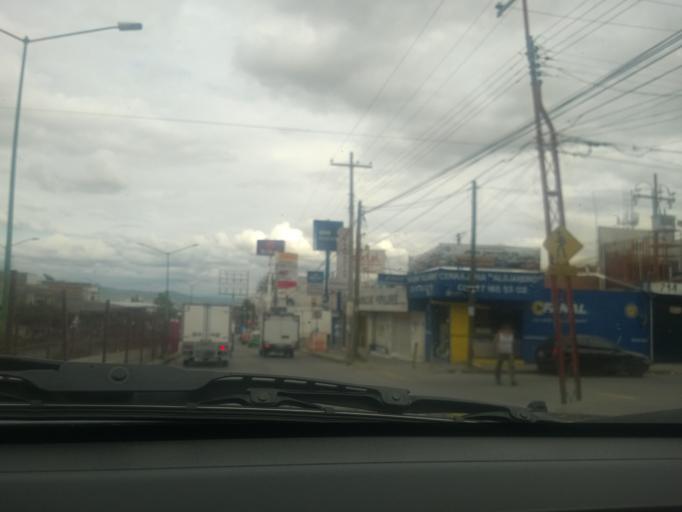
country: MX
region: Guanajuato
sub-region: Leon
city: La Ermita
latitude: 21.1312
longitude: -101.7057
